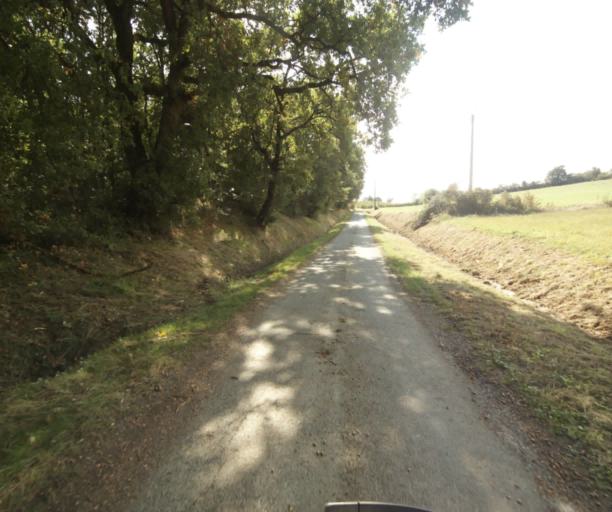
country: FR
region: Midi-Pyrenees
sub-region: Departement du Tarn-et-Garonne
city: Finhan
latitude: 43.8803
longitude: 1.1871
